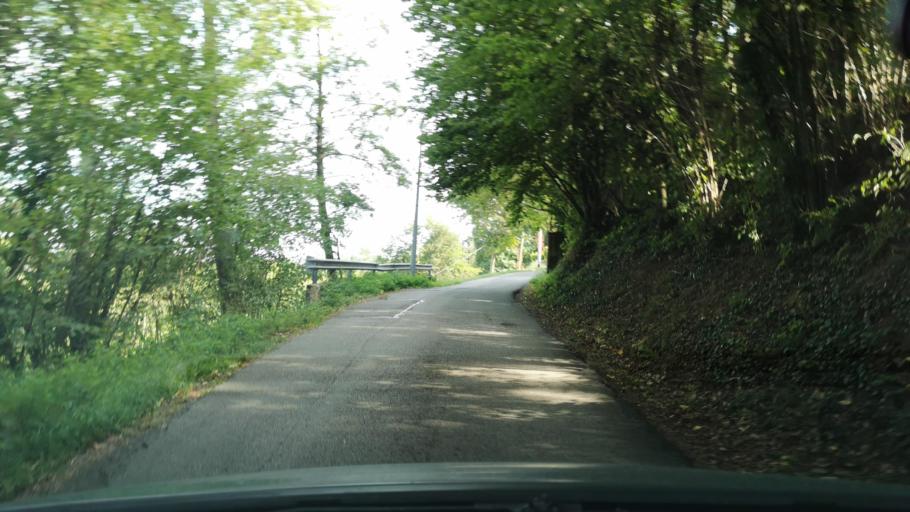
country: IT
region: Piedmont
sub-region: Provincia di Torino
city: Corio
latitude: 45.3105
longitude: 7.5262
